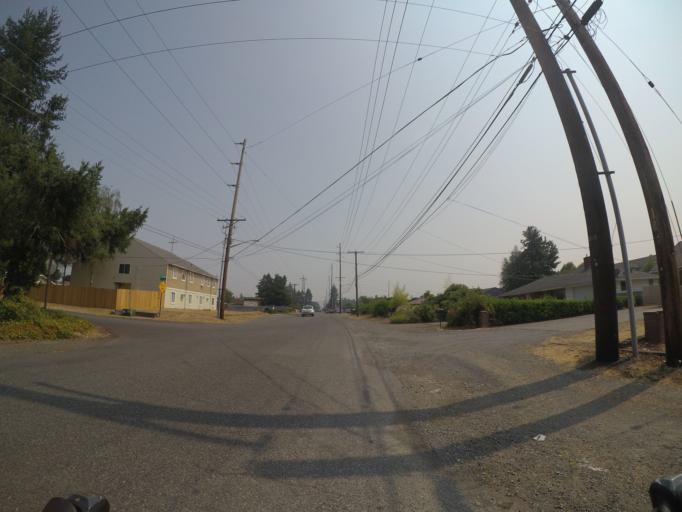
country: US
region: Washington
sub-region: Pierce County
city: Lakewood
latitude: 47.1565
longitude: -122.5075
